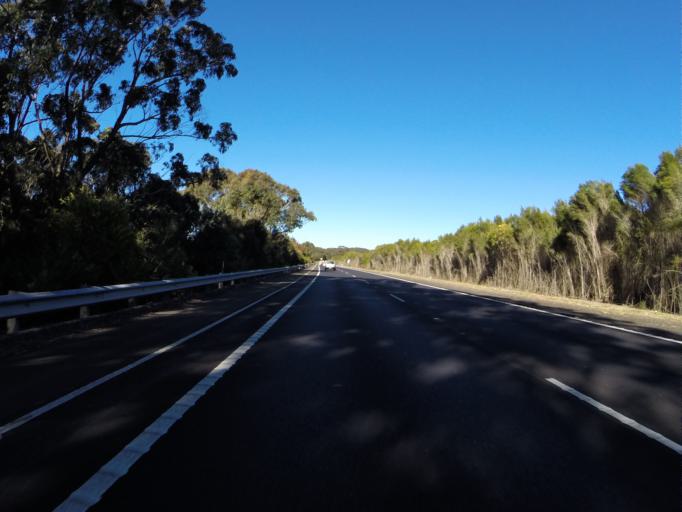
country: AU
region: New South Wales
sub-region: Wollongong
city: Helensburgh
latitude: -34.2315
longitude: 150.9472
